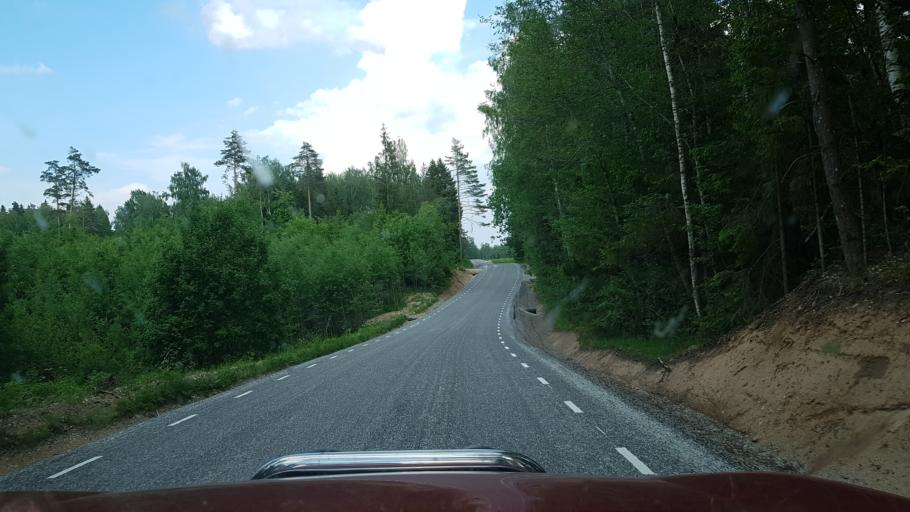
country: EE
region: Tartu
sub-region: UElenurme vald
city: Ulenurme
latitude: 58.1017
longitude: 26.7849
